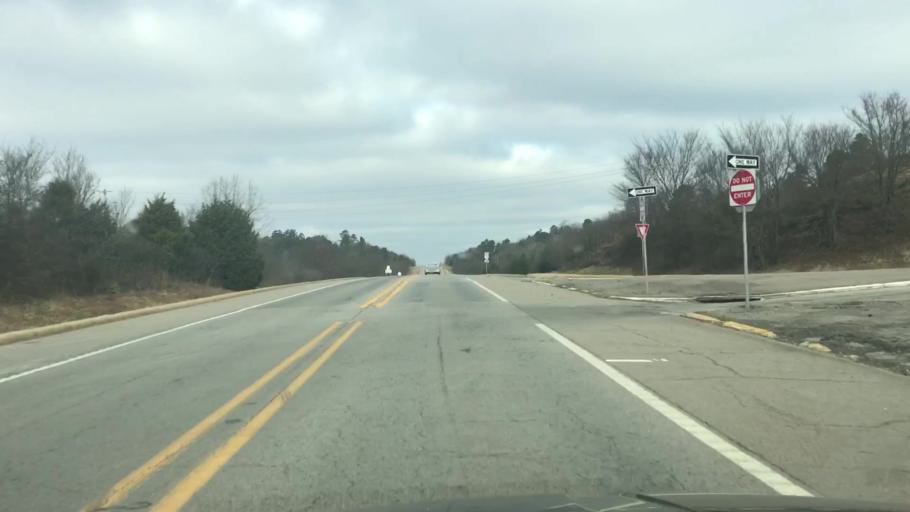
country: US
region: Arkansas
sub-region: Scott County
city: Waldron
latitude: 34.8563
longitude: -94.0672
